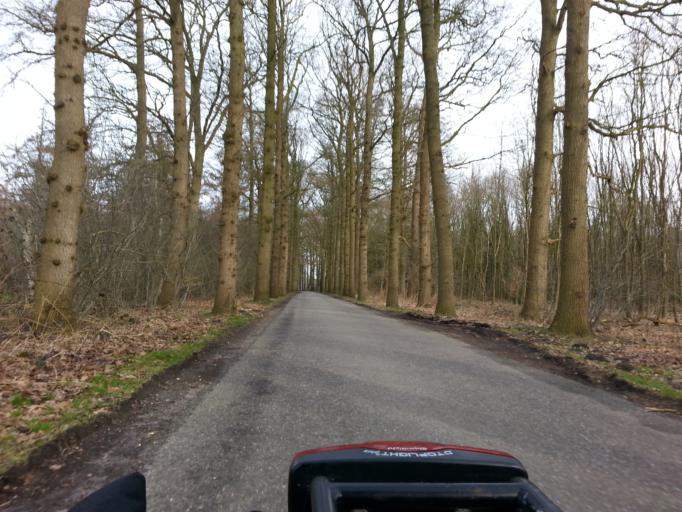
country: NL
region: Utrecht
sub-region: Gemeente Woudenberg
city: Woudenberg
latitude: 52.0881
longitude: 5.3895
